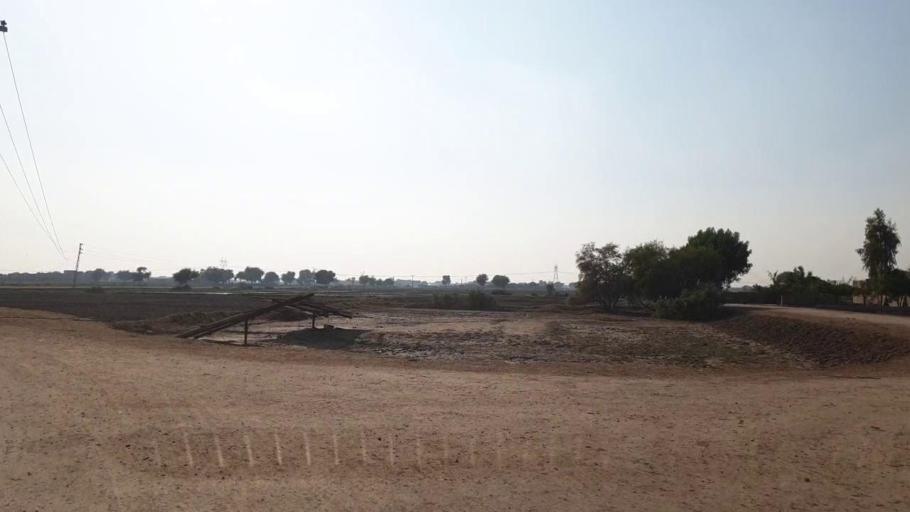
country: PK
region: Sindh
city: Sehwan
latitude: 26.4410
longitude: 67.8073
